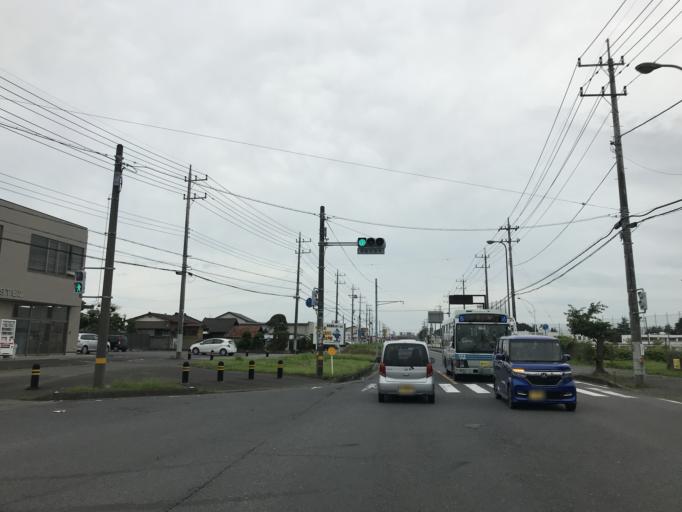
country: JP
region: Ibaraki
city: Mito-shi
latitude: 36.3256
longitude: 140.4574
